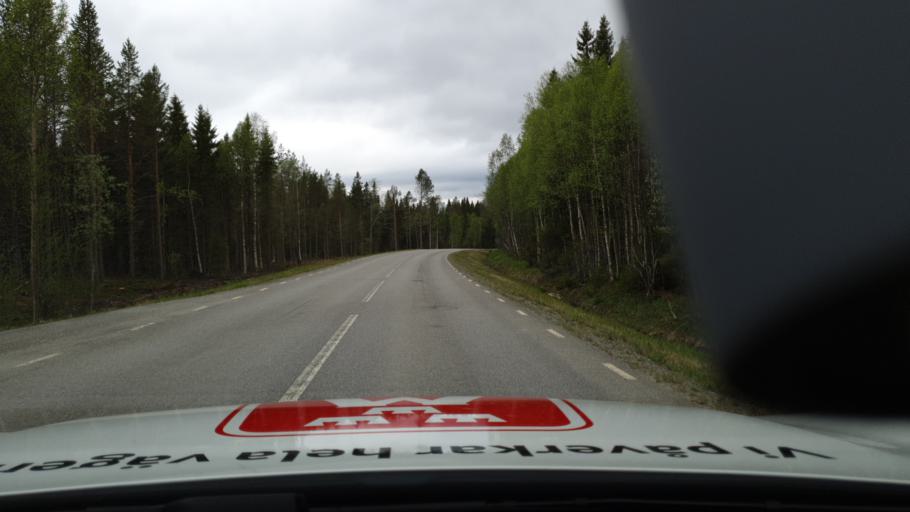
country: NO
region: Nord-Trondelag
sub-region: Lierne
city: Sandvika
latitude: 64.4778
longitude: 14.0958
